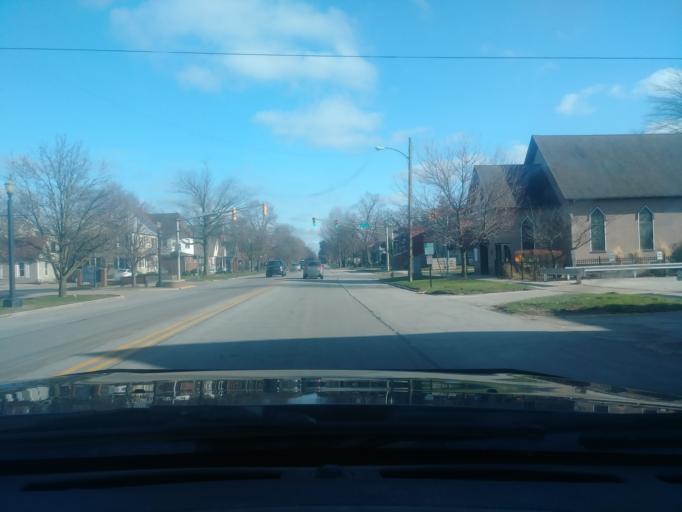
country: US
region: Indiana
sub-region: LaPorte County
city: LaPorte
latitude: 41.6097
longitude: -86.7215
